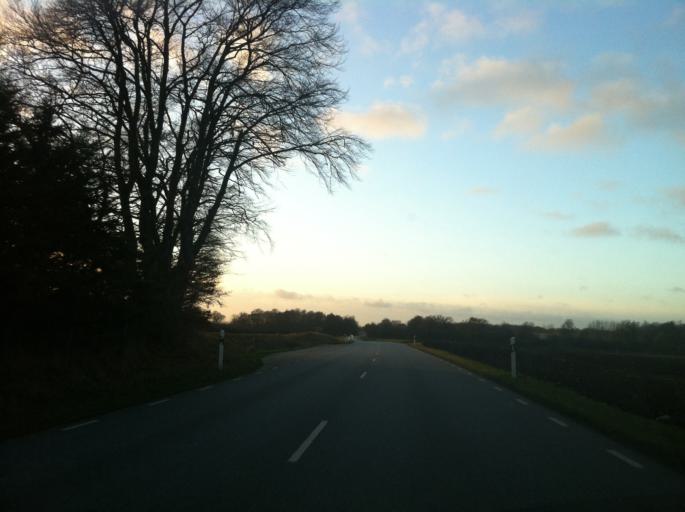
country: SE
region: Skane
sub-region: Hoors Kommun
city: Hoeoer
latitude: 55.9397
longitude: 13.5110
